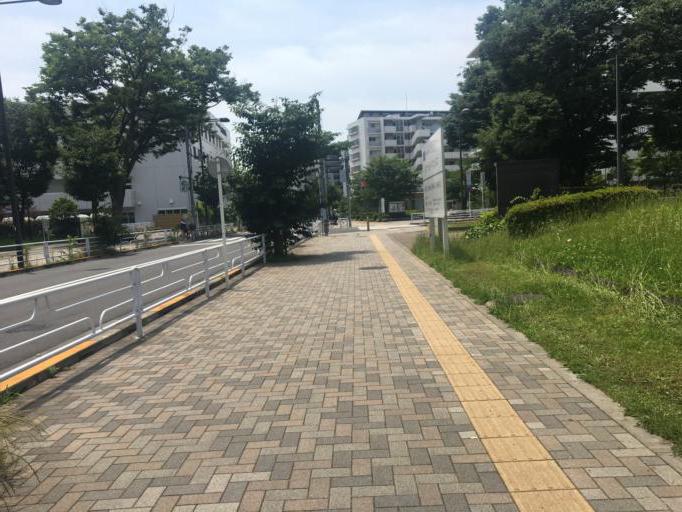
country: JP
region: Tokyo
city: Tanashicho
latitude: 35.7453
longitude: 139.5365
